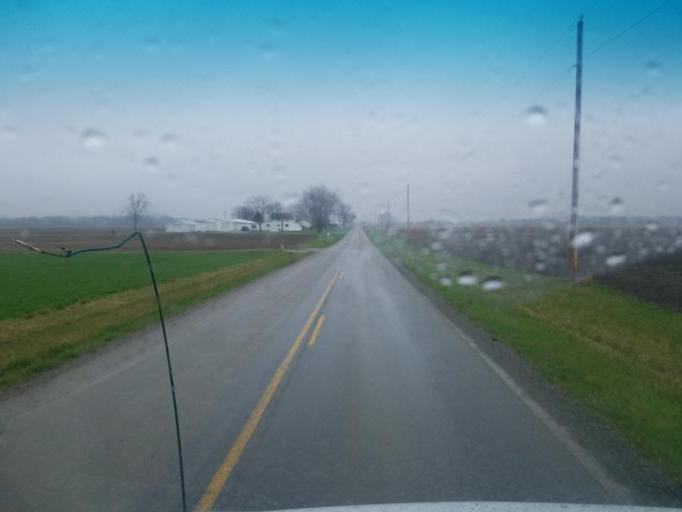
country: US
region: Ohio
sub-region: Wyandot County
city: Carey
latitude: 40.9854
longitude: -83.2911
